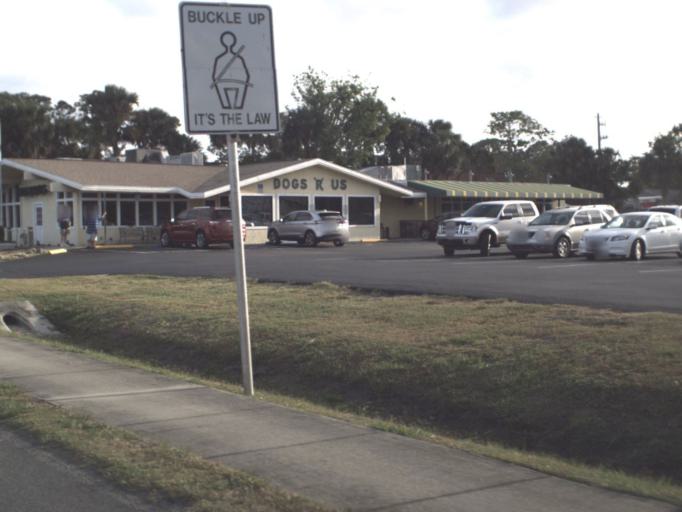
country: US
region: Florida
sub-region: Brevard County
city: Titusville
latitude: 28.5660
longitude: -80.7984
